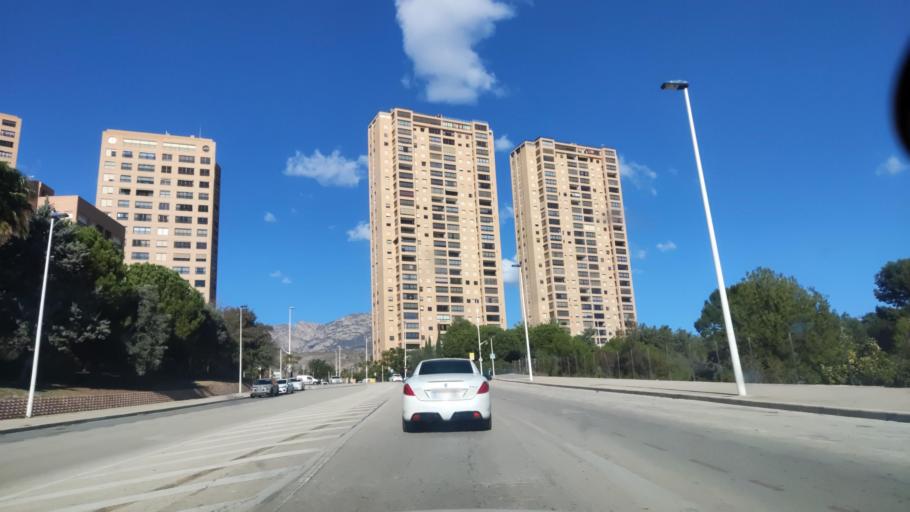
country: ES
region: Valencia
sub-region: Provincia de Alicante
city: Benidorm
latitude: 38.5355
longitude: -0.1568
